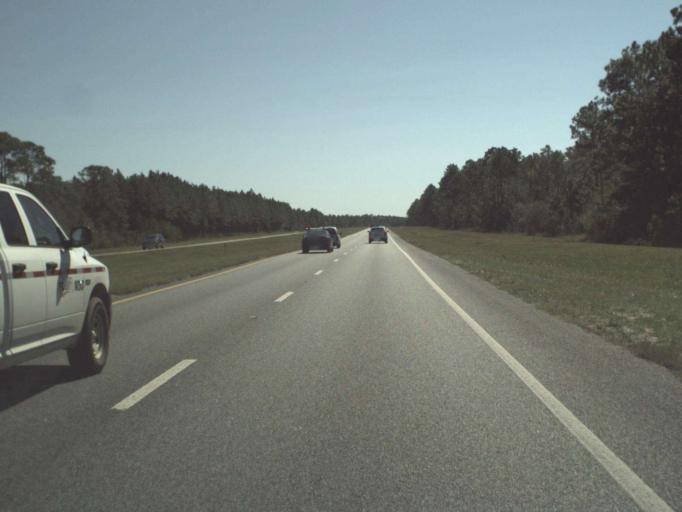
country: US
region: Florida
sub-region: Walton County
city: Seaside
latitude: 30.3372
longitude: -86.0643
